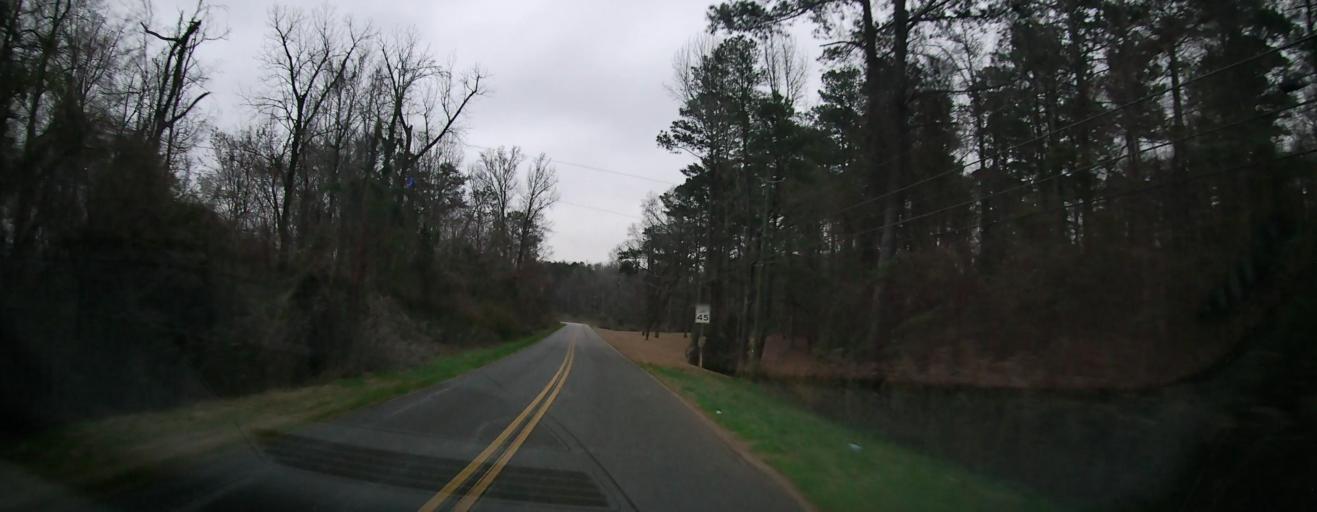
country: US
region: Georgia
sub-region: Bibb County
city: West Point
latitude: 32.8986
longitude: -83.7735
